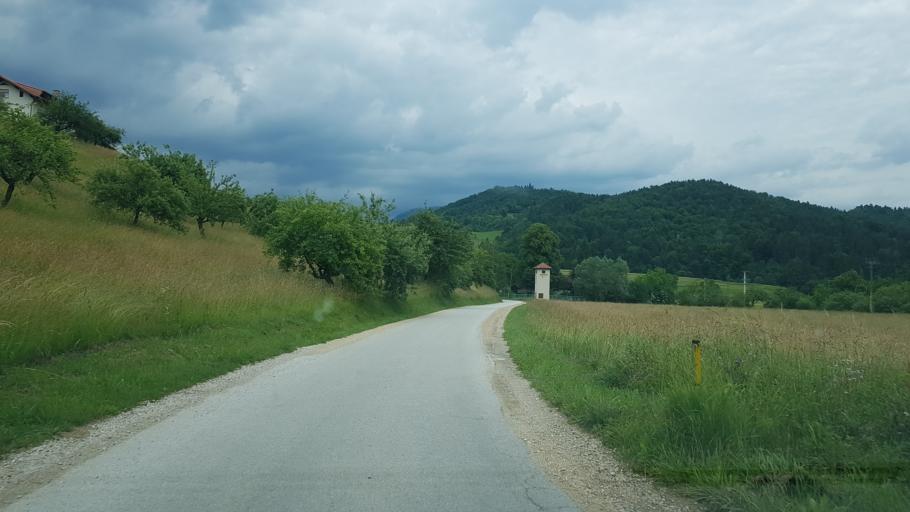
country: SI
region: Dobrna
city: Dobrna
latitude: 46.3404
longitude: 15.2705
